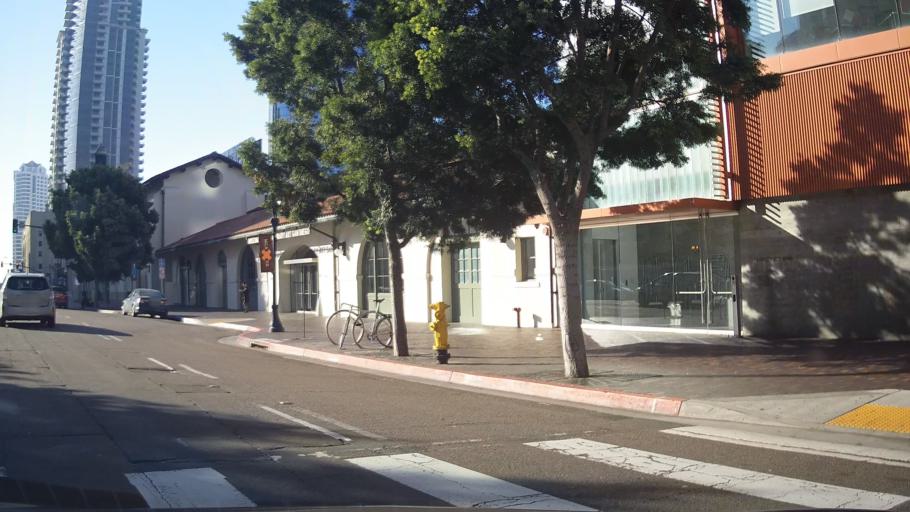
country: US
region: California
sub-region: San Diego County
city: San Diego
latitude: 32.7177
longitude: -117.1692
